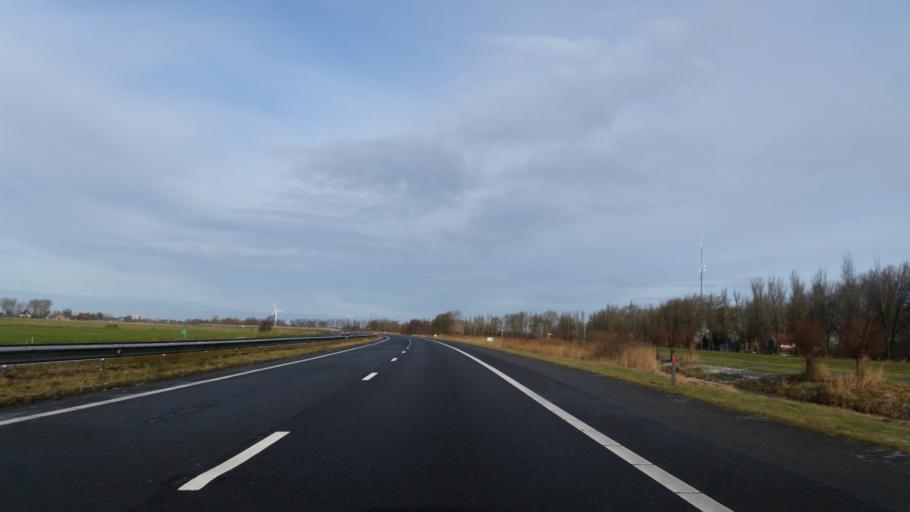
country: NL
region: Friesland
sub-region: Gemeente Boarnsterhim
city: Nes
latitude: 53.0182
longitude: 5.8683
